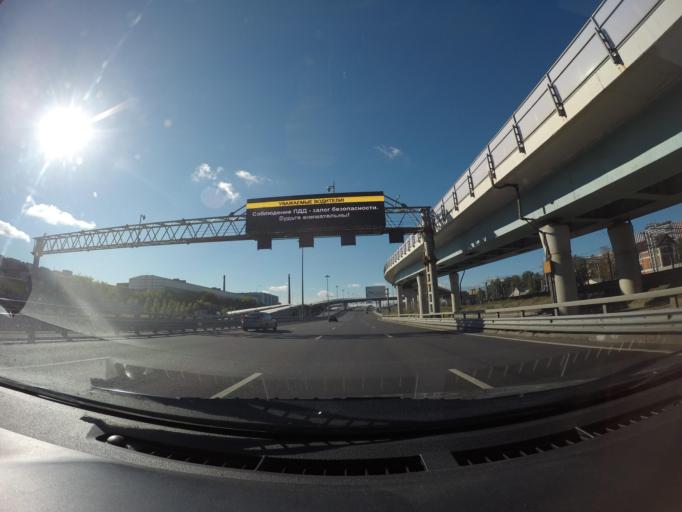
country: RU
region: Moscow
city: Ryazanskiy
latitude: 55.7637
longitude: 37.7474
